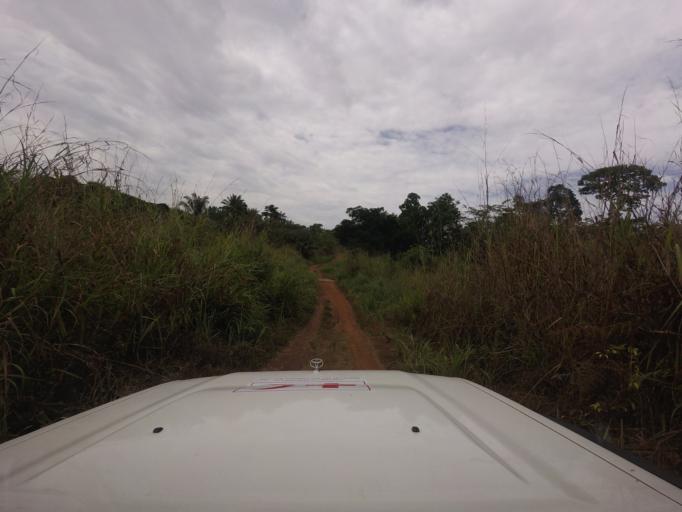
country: SL
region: Eastern Province
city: Buedu
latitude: 8.2654
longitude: -10.2410
